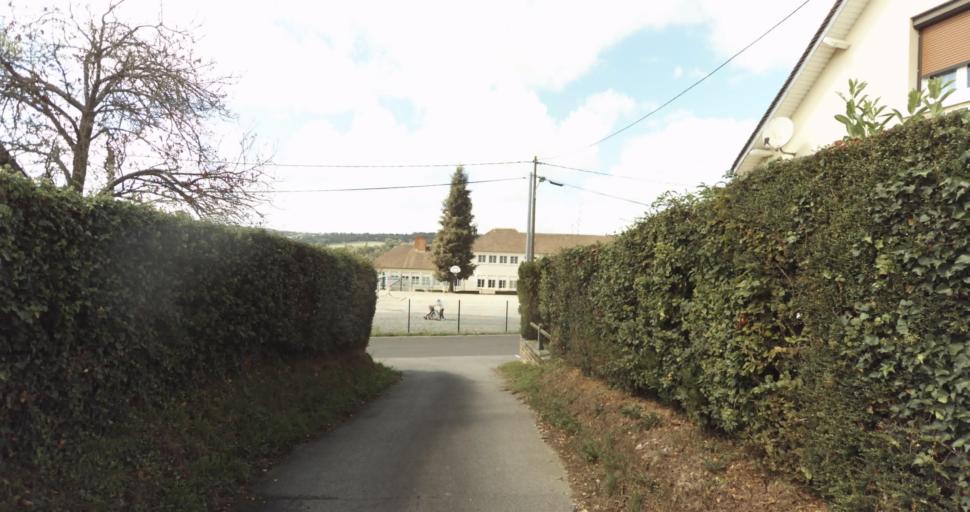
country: FR
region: Lower Normandy
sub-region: Departement de l'Orne
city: Gace
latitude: 48.7910
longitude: 0.2984
